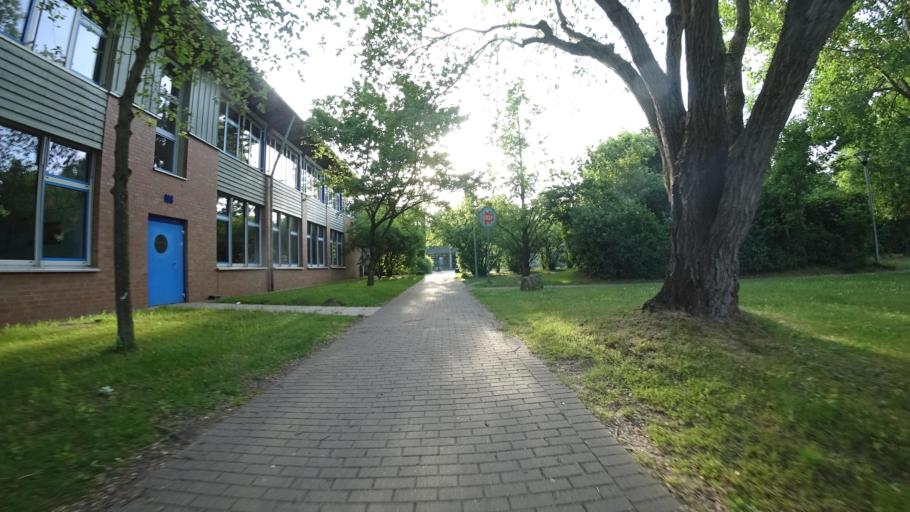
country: DE
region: North Rhine-Westphalia
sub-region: Regierungsbezirk Detmold
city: Guetersloh
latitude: 51.9009
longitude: 8.4083
